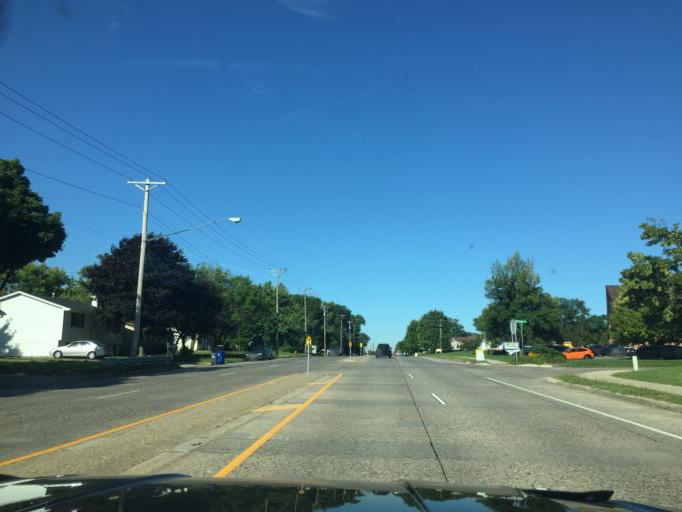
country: US
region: Minnesota
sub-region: Ramsey County
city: Roseville
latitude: 44.9920
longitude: -93.1389
